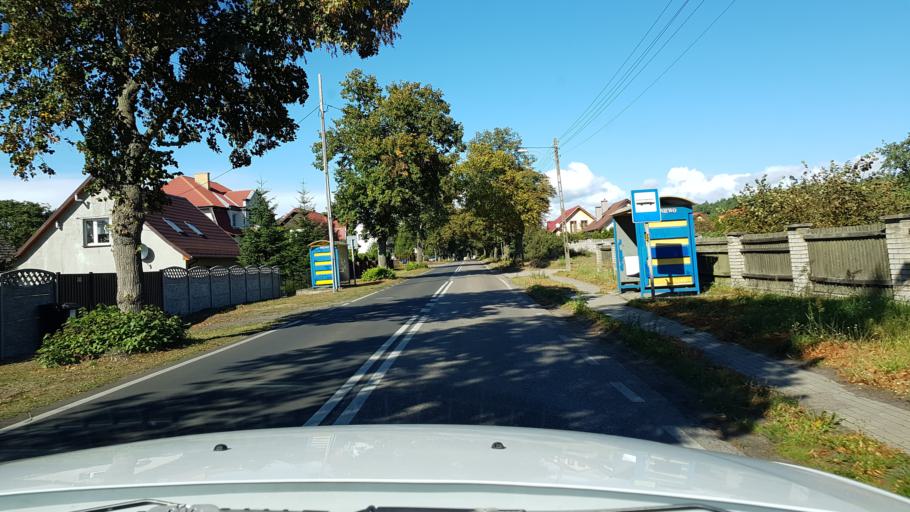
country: PL
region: West Pomeranian Voivodeship
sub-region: Powiat gryfinski
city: Gryfino
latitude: 53.2061
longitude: 14.5017
